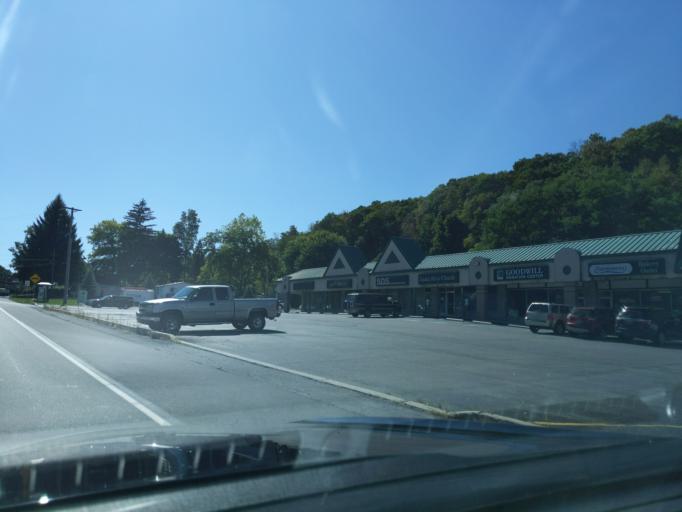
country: US
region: Pennsylvania
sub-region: Blair County
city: Greenwood
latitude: 40.5345
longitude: -78.3590
